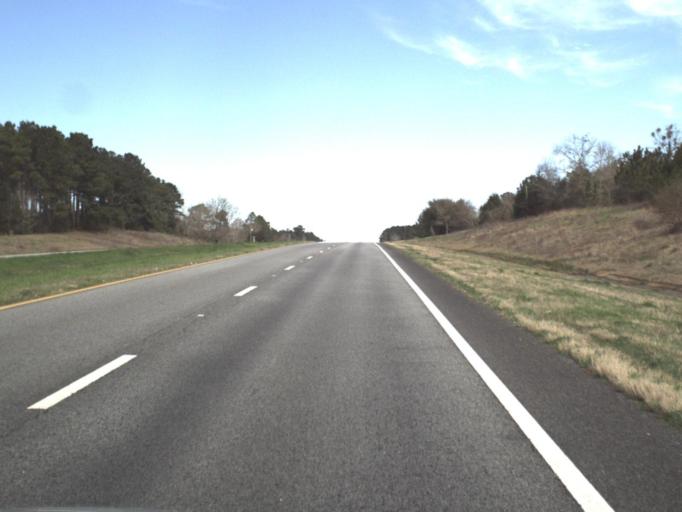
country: US
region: Florida
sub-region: Jackson County
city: Marianna
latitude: 30.8254
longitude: -85.3611
